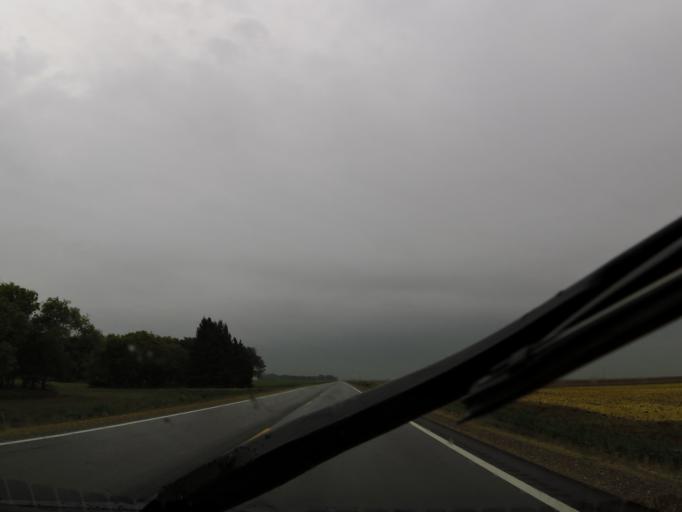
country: US
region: Minnesota
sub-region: Marshall County
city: Warren
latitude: 48.4563
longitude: -96.9444
